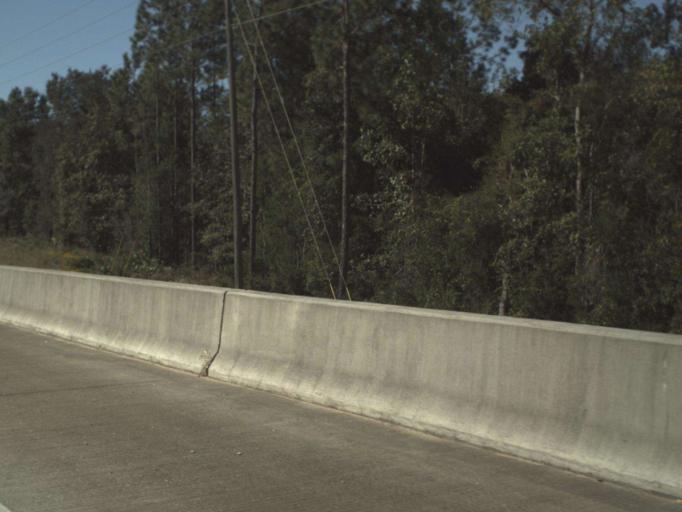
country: US
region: Florida
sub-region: Walton County
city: Freeport
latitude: 30.4962
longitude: -86.1195
